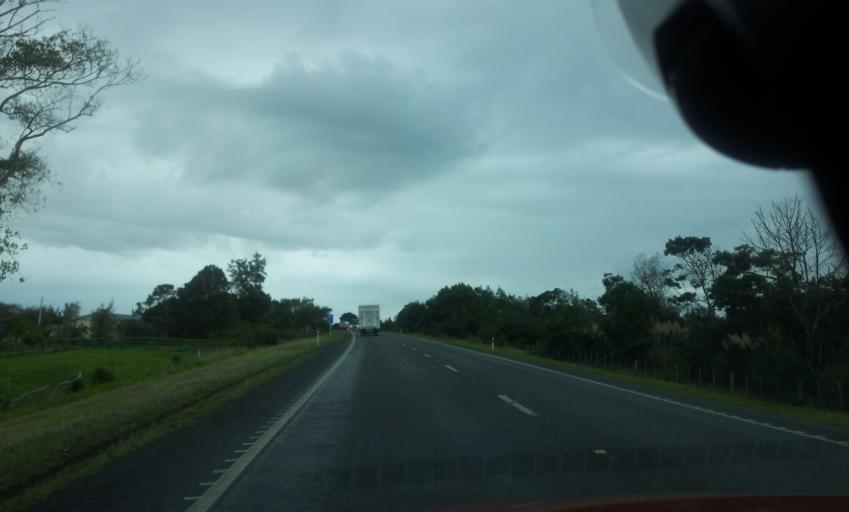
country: NZ
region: Northland
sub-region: Whangarei
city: Ruakaka
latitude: -35.9405
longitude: 174.4560
